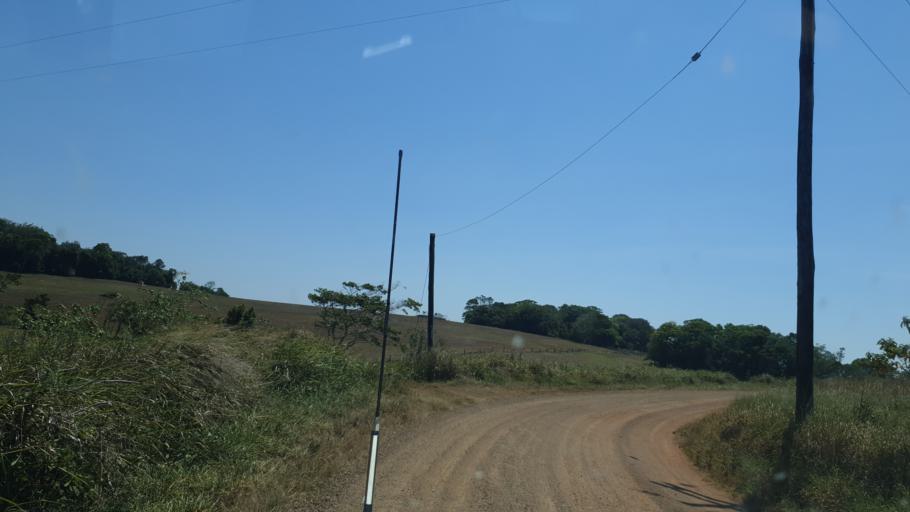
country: AU
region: Queensland
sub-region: Tablelands
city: Atherton
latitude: -17.3499
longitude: 145.6211
